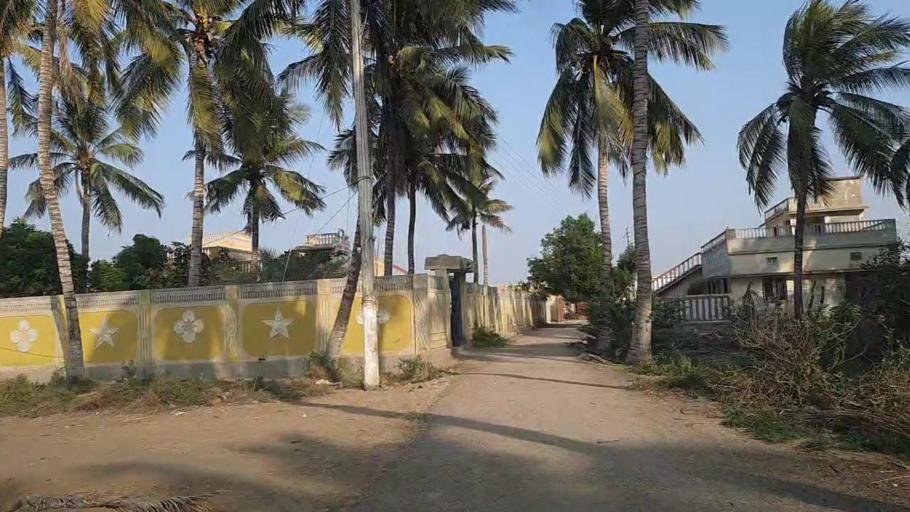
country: PK
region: Sindh
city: Keti Bandar
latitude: 24.1642
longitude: 67.6295
